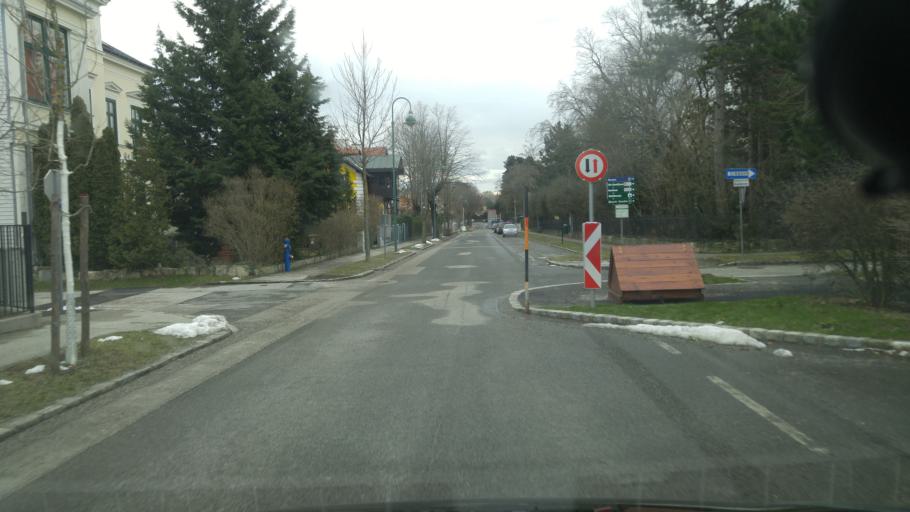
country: AT
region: Lower Austria
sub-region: Politischer Bezirk Baden
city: Bad Voslau
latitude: 47.9723
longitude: 16.2125
